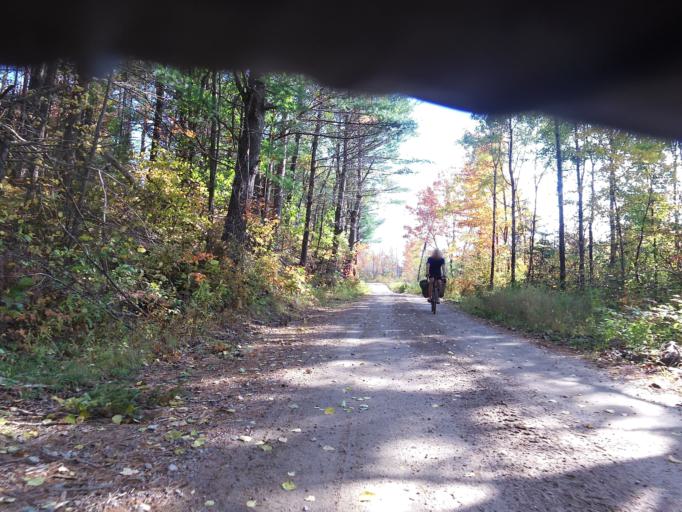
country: CA
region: Ontario
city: Petawawa
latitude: 45.7998
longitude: -77.3171
